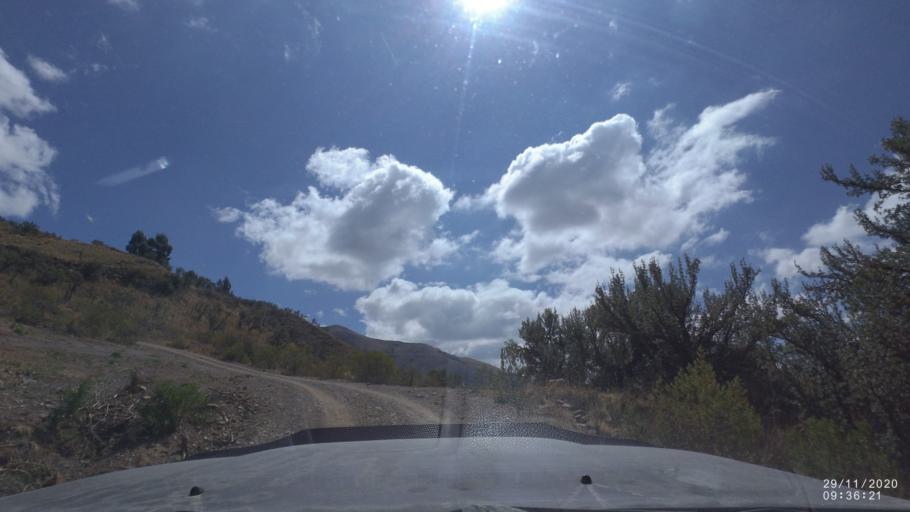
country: BO
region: Cochabamba
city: Cochabamba
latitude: -17.3098
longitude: -66.1876
